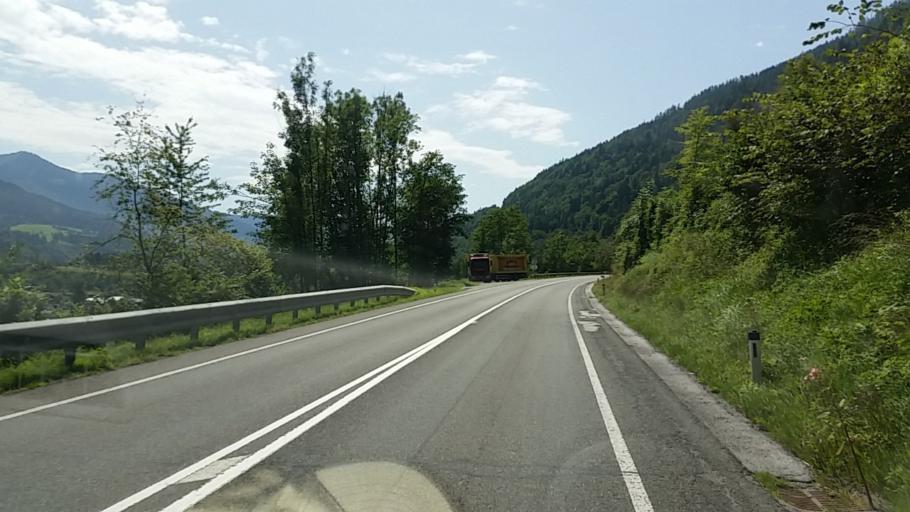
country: AT
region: Salzburg
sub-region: Politischer Bezirk Sankt Johann im Pongau
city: Pfarrwerfen
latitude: 47.4425
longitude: 13.2096
